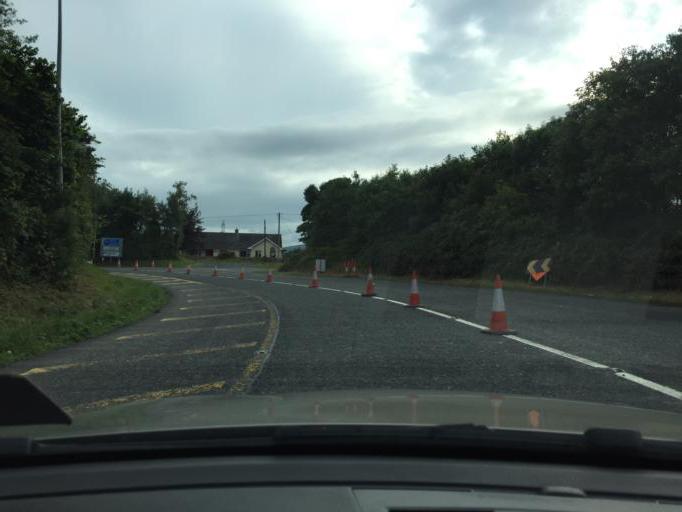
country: IE
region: Leinster
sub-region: Wicklow
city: Arklow
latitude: 52.8229
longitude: -6.1457
